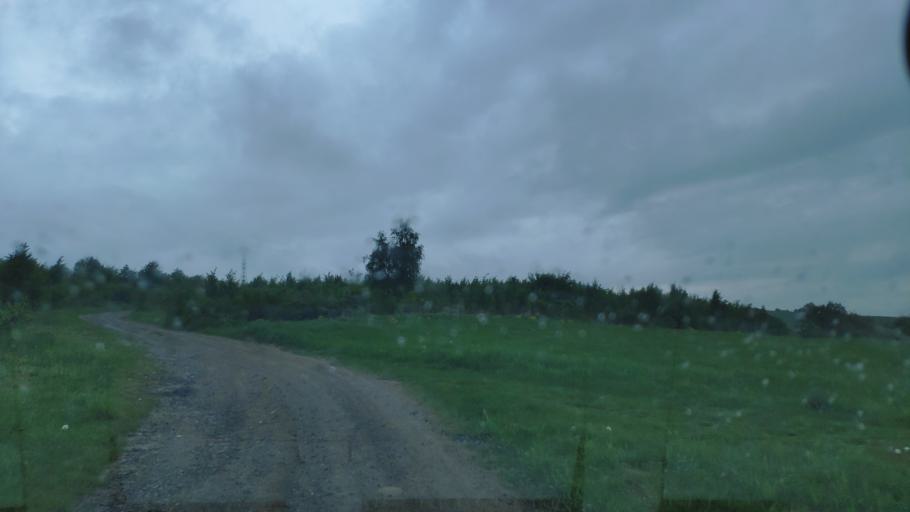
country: SK
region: Kosicky
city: Kosice
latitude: 48.7612
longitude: 21.2018
